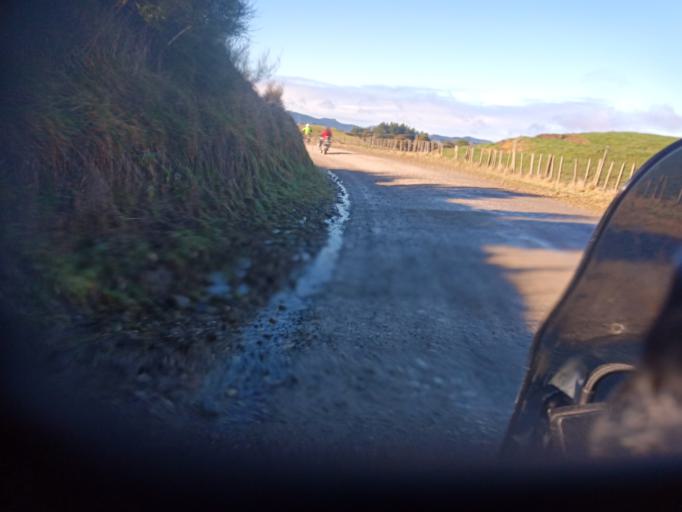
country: NZ
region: Gisborne
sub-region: Gisborne District
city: Gisborne
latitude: -38.2011
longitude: 178.0670
